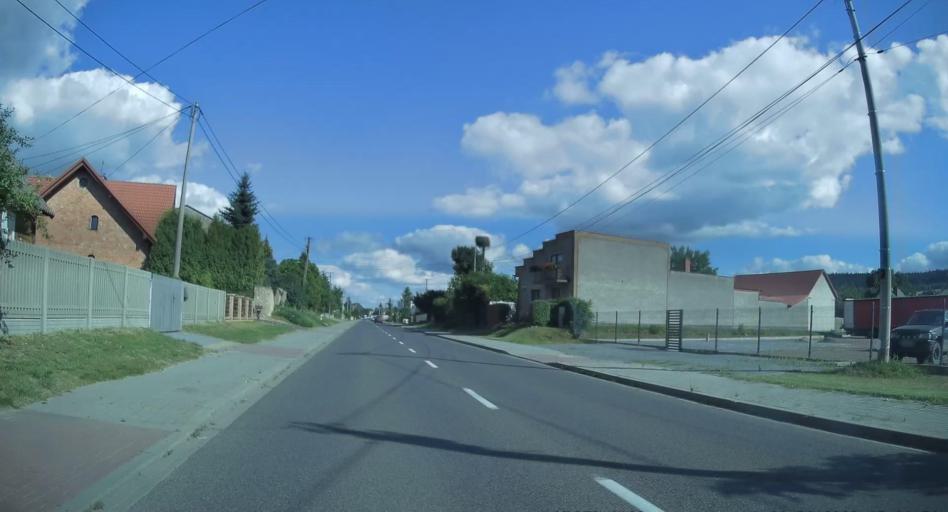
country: PL
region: Swietokrzyskie
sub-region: Powiat kielecki
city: Bodzentyn
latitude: 50.9456
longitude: 20.9387
